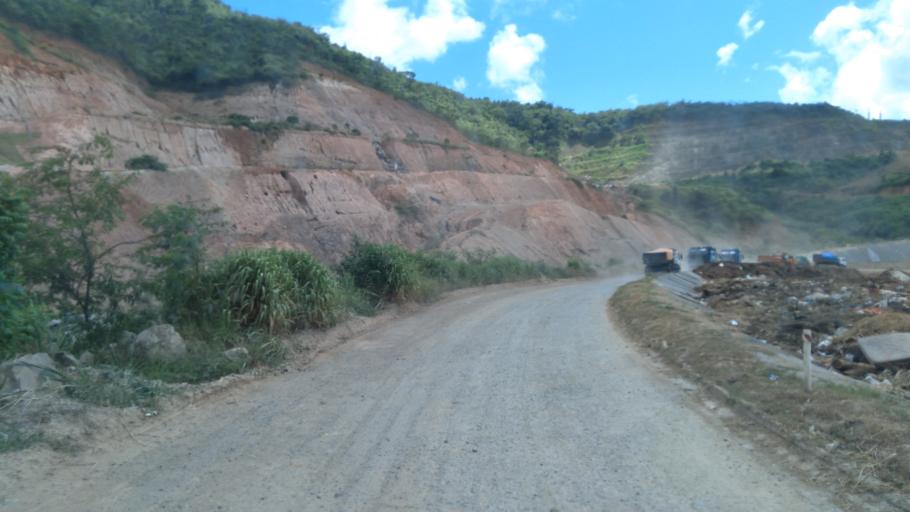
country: BR
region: Minas Gerais
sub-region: Santa Luzia
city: Santa Luzia
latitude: -19.8512
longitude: -43.8498
